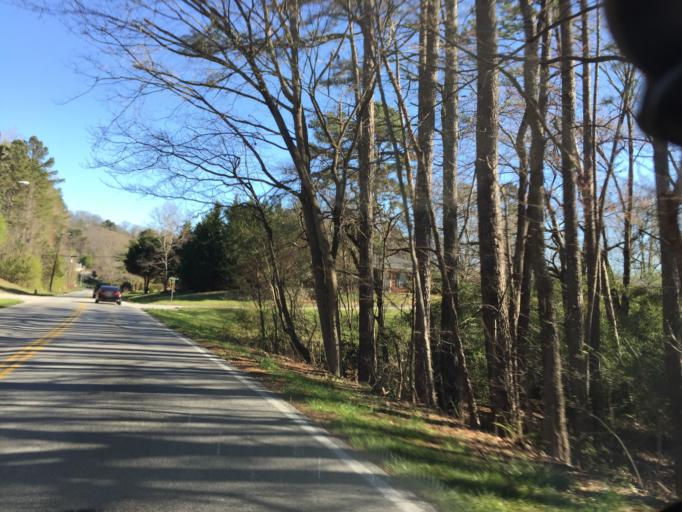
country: US
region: Tennessee
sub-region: Hamilton County
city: East Chattanooga
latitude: 35.1157
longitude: -85.2119
